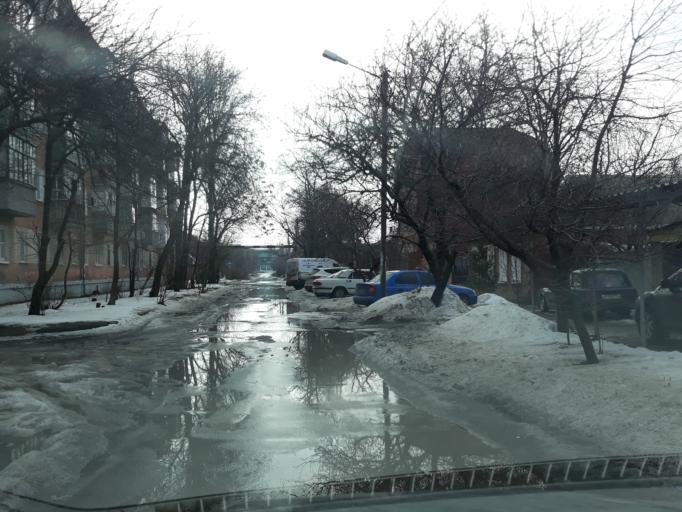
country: RU
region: Rostov
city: Taganrog
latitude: 47.2205
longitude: 38.8863
